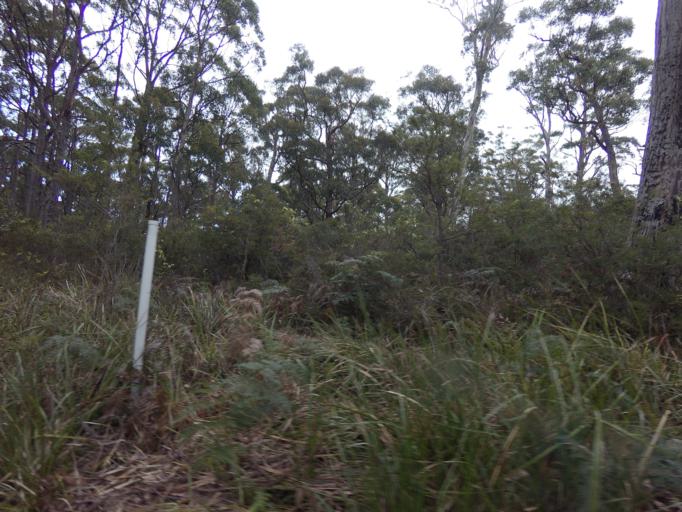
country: AU
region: Tasmania
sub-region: Huon Valley
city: Geeveston
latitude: -43.4657
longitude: 146.9299
